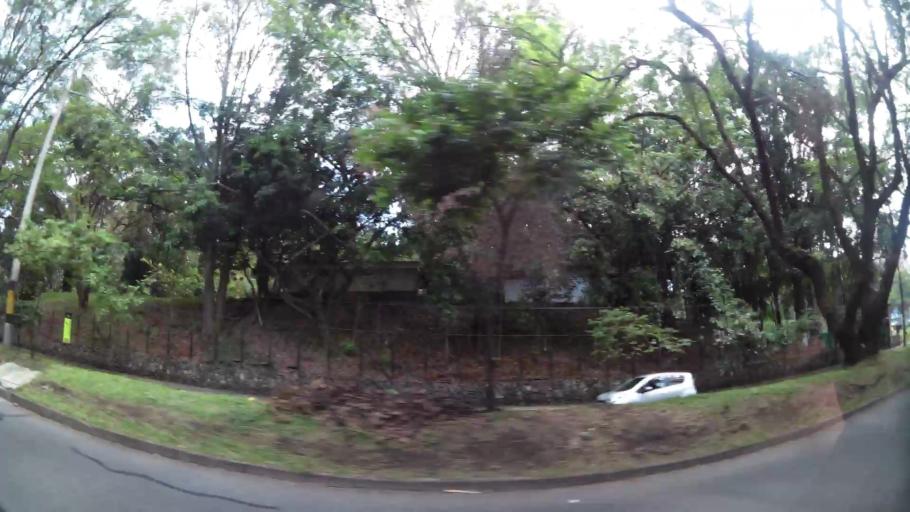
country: CO
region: Antioquia
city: Envigado
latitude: 6.1864
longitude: -75.5783
